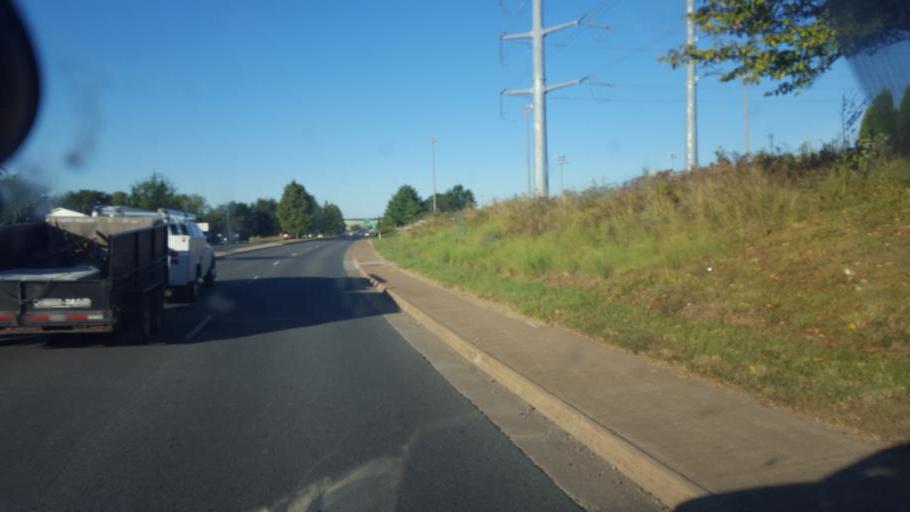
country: US
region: Virginia
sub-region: City of Manassas
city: Manassas
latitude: 38.7457
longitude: -77.5085
